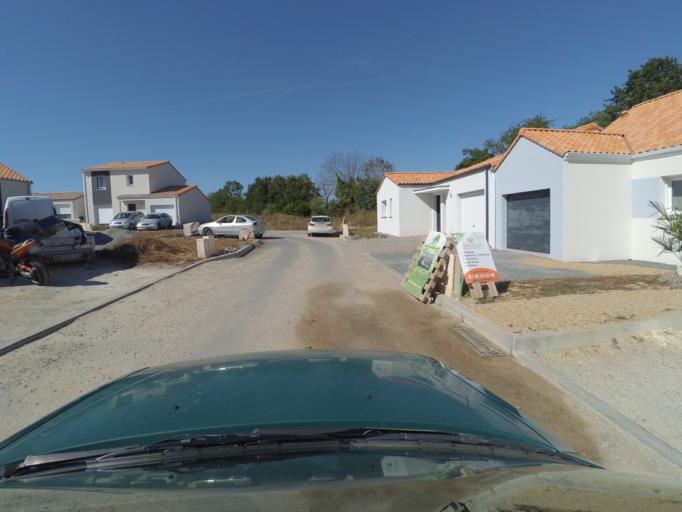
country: FR
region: Pays de la Loire
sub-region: Departement de la Loire-Atlantique
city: Aigrefeuille-sur-Maine
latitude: 47.0853
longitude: -1.4080
